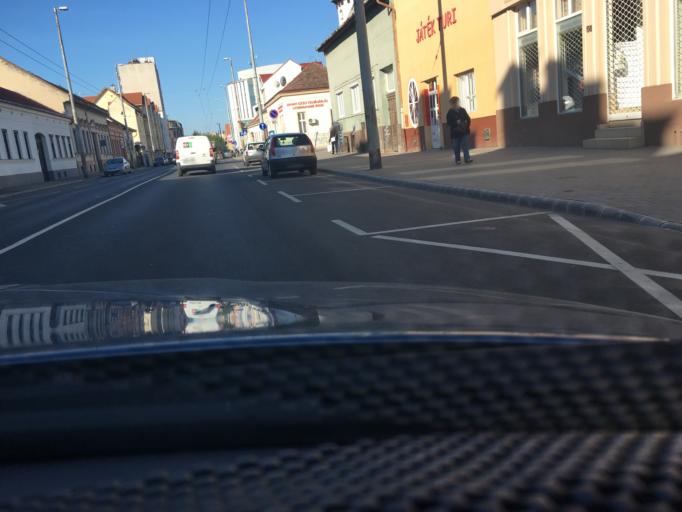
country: HU
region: Hajdu-Bihar
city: Debrecen
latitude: 47.5340
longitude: 21.6326
